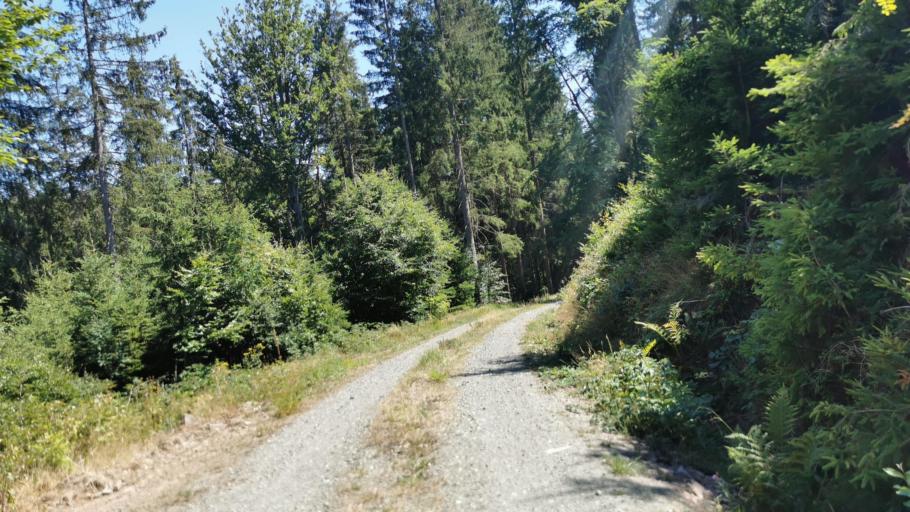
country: DE
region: Bavaria
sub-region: Upper Franconia
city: Pressig
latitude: 50.4018
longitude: 11.2871
